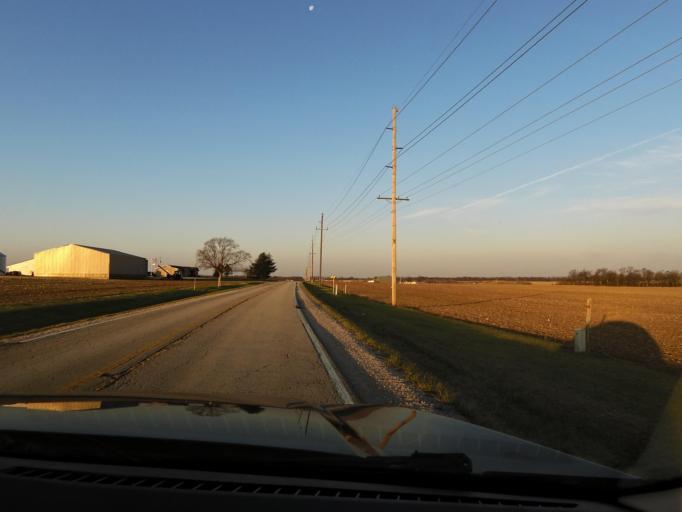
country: US
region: Illinois
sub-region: Marion County
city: Odin
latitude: 38.7650
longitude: -89.0319
